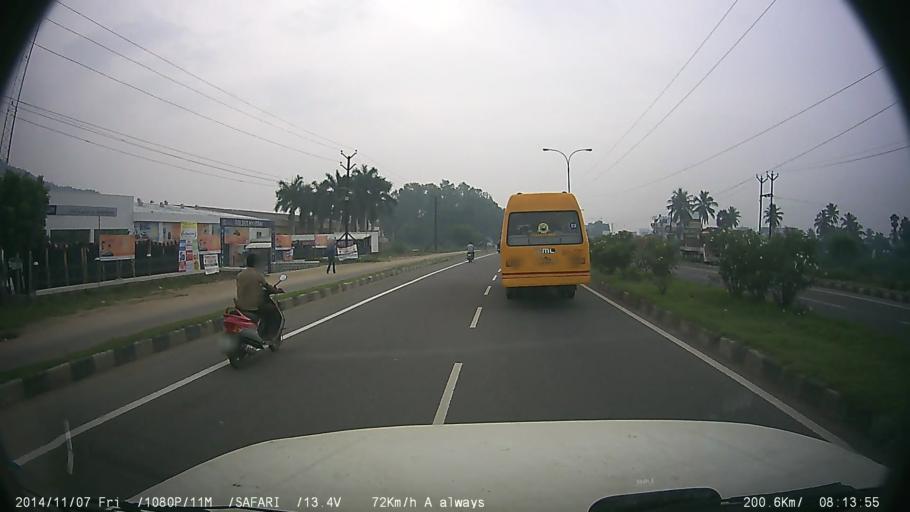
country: IN
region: Tamil Nadu
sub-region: Salem
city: Salem
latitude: 11.6902
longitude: 78.1167
